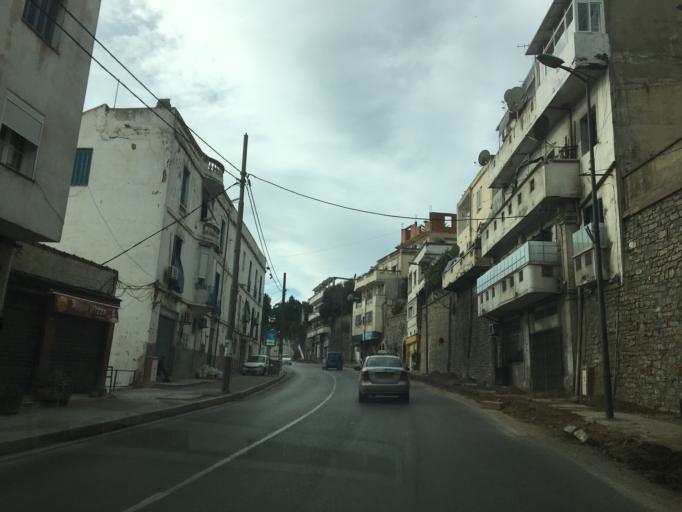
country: DZ
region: Alger
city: Algiers
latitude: 36.7725
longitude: 3.0416
